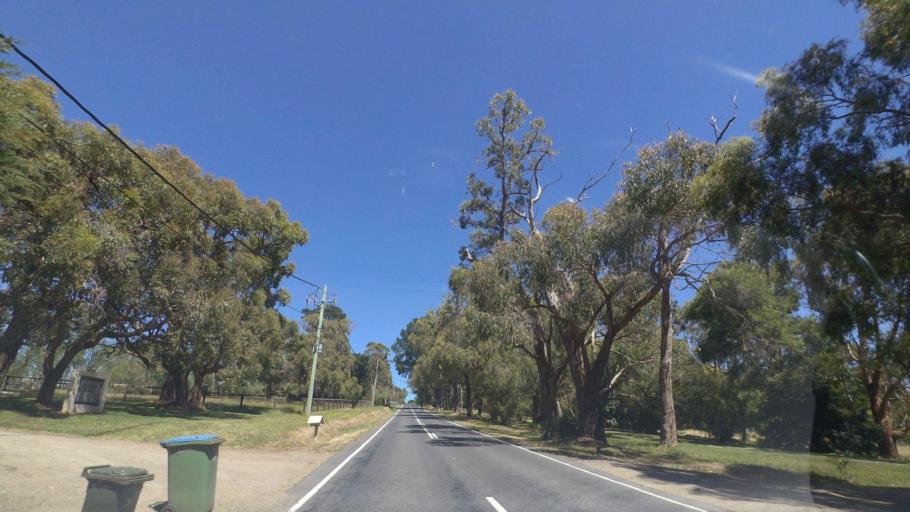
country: AU
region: Victoria
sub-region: Mornington Peninsula
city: Merricks
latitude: -38.3741
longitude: 145.0582
